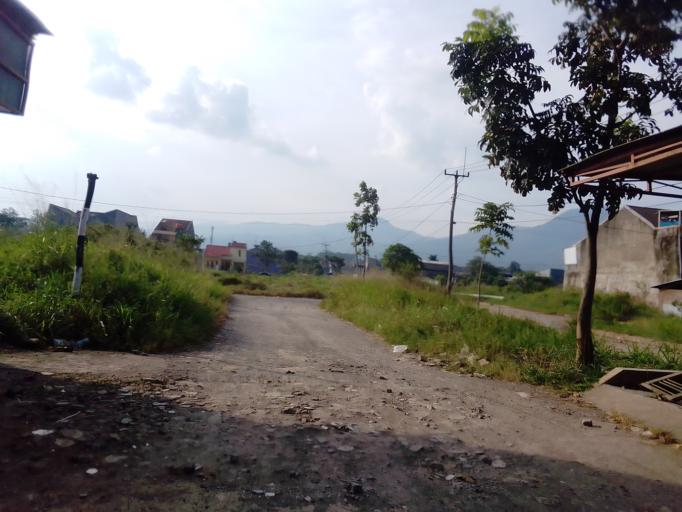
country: ID
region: West Java
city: Cileunyi
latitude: -6.9351
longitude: 107.7135
